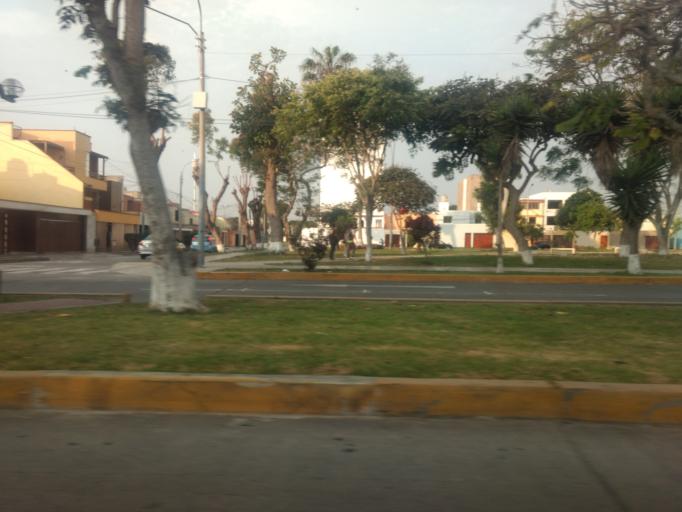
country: PE
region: Callao
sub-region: Callao
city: Callao
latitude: -12.0737
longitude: -77.1051
